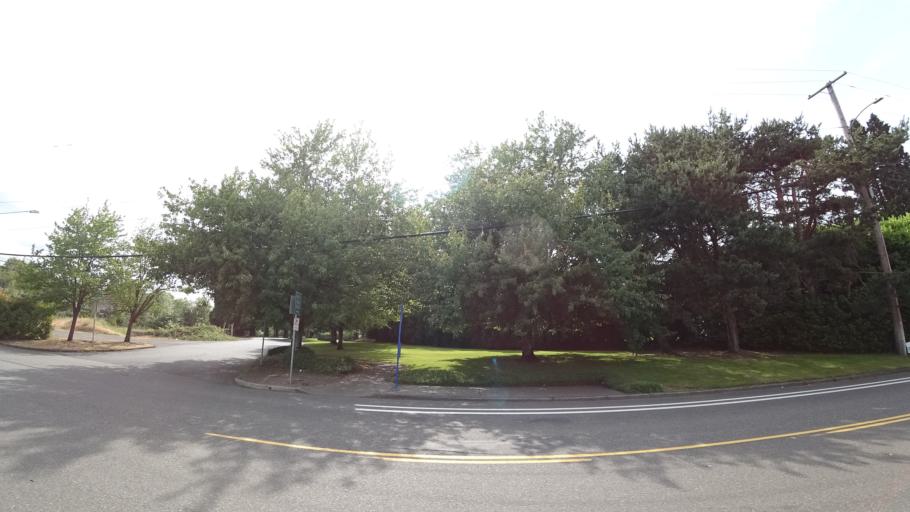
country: US
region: Washington
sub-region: Clark County
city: Vancouver
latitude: 45.5820
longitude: -122.6331
